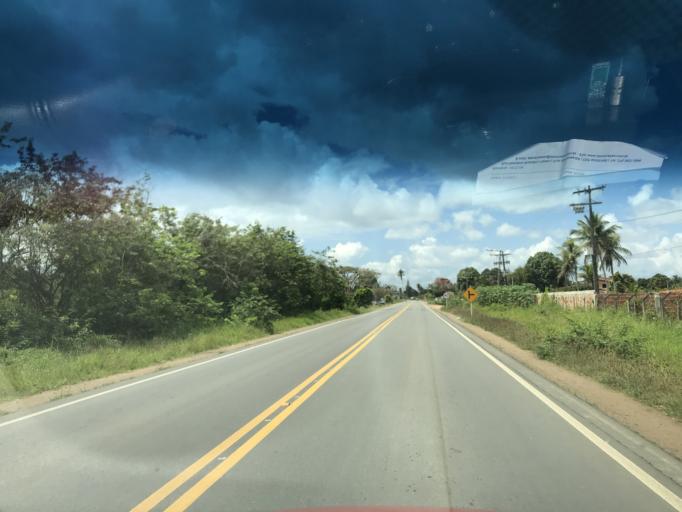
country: BR
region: Bahia
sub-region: Conceicao Do Almeida
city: Conceicao do Almeida
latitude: -12.7293
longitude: -39.1981
